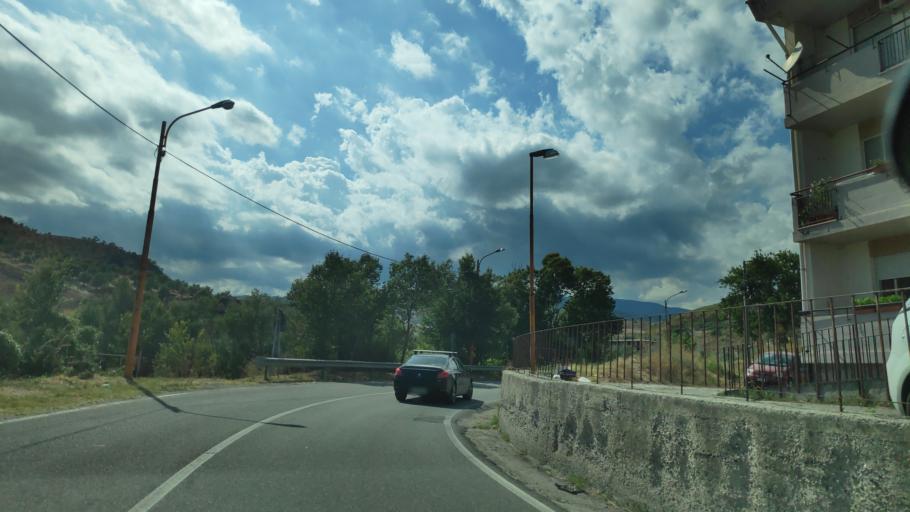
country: IT
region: Calabria
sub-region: Provincia di Catanzaro
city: Santa Caterina dello Ionio Marina
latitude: 38.5269
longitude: 16.5667
